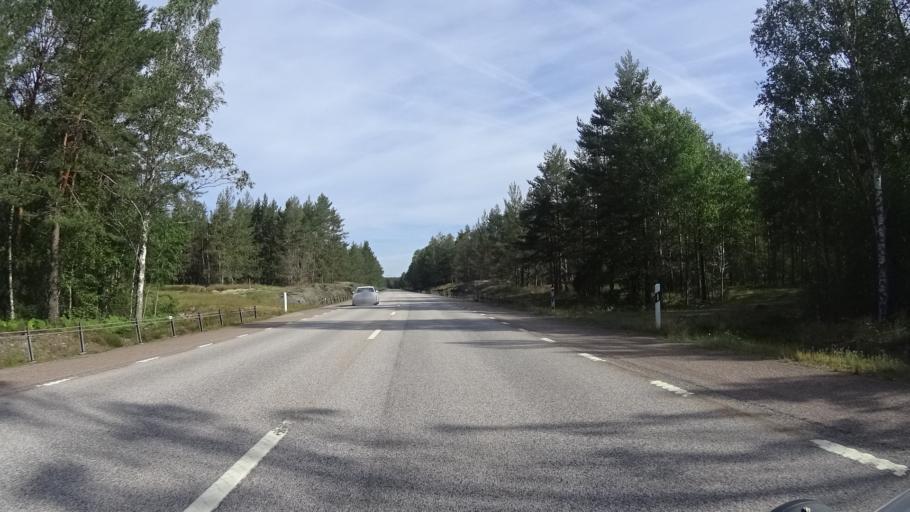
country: SE
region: Kalmar
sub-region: Oskarshamns Kommun
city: Oskarshamn
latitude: 57.5104
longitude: 16.5016
